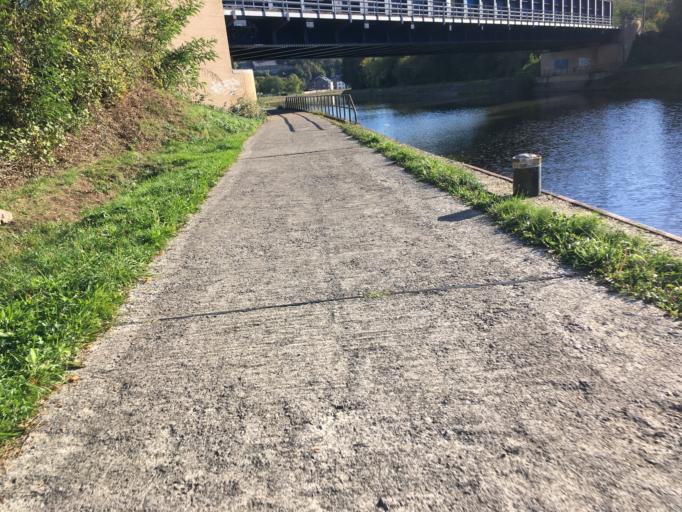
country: BE
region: Wallonia
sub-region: Province de Namur
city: Floreffe
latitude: 50.4405
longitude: 4.7576
